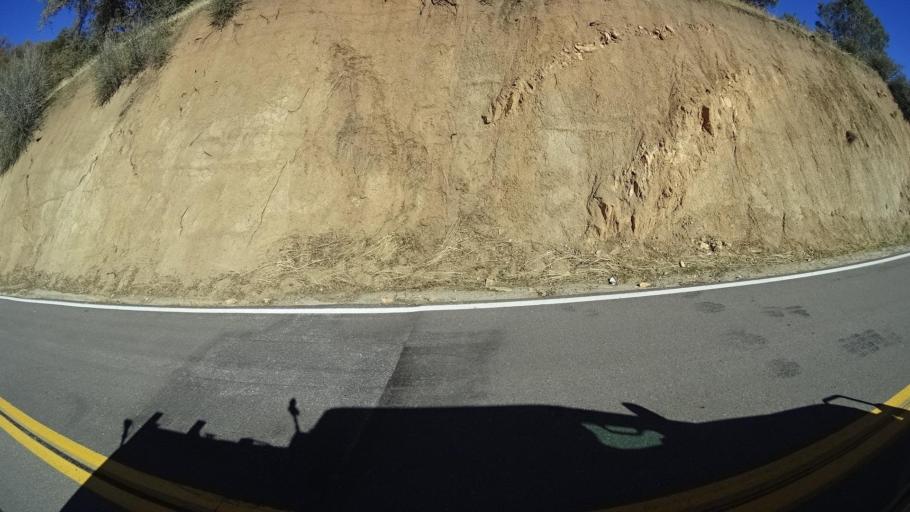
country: US
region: California
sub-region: Kern County
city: Alta Sierra
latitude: 35.7412
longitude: -118.6077
